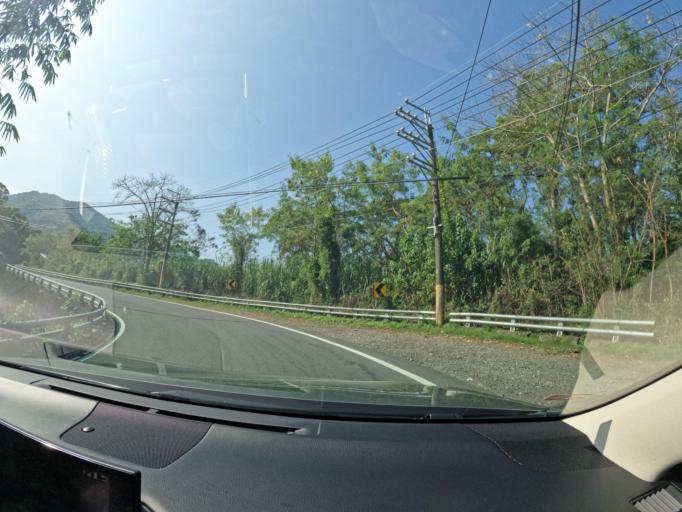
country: TW
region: Taiwan
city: Yujing
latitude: 23.0799
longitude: 120.6062
